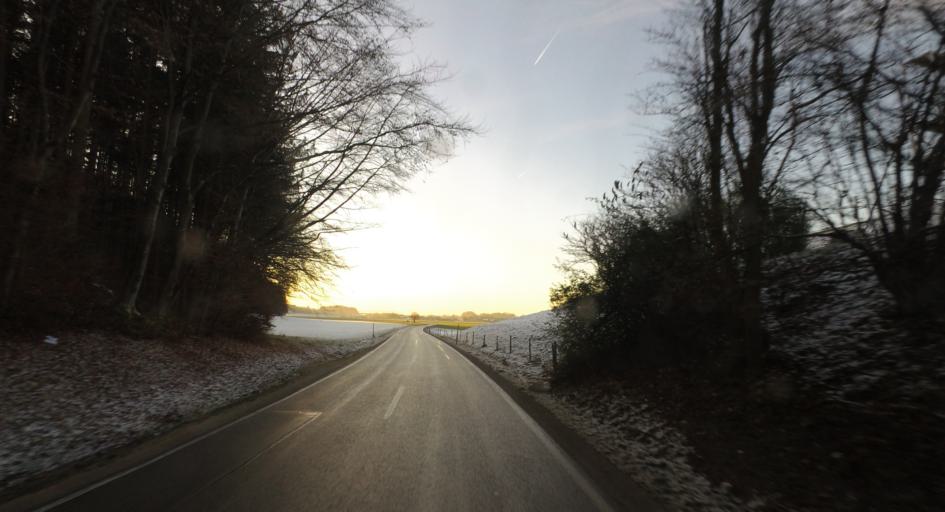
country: DE
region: Bavaria
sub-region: Upper Bavaria
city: Nussdorf
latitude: 47.8872
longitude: 12.5914
